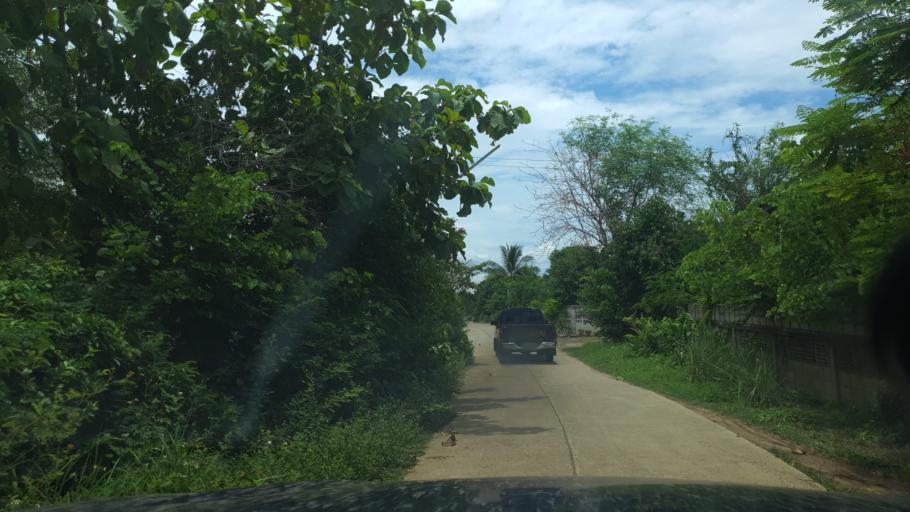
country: TH
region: Lampang
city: Soem Ngam
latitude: 18.0952
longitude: 99.3425
